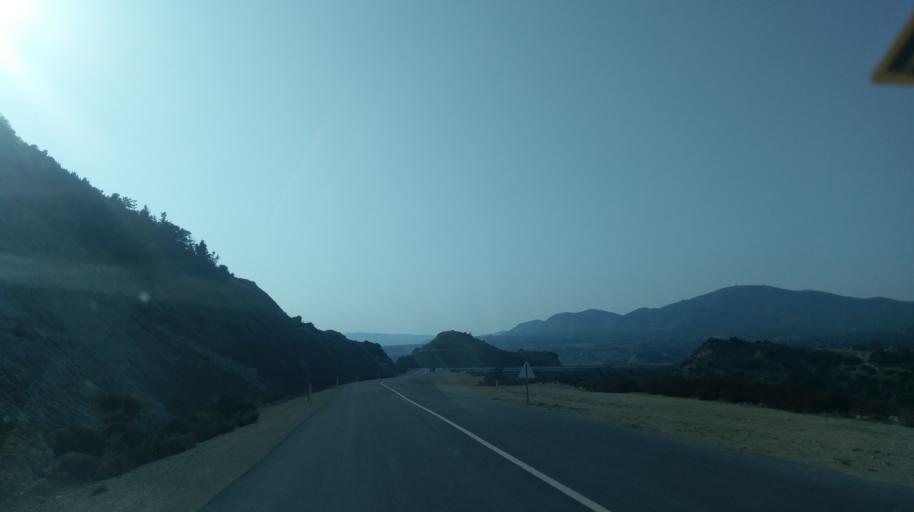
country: CY
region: Ammochostos
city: Rizokarpaso
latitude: 35.5228
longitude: 34.2941
